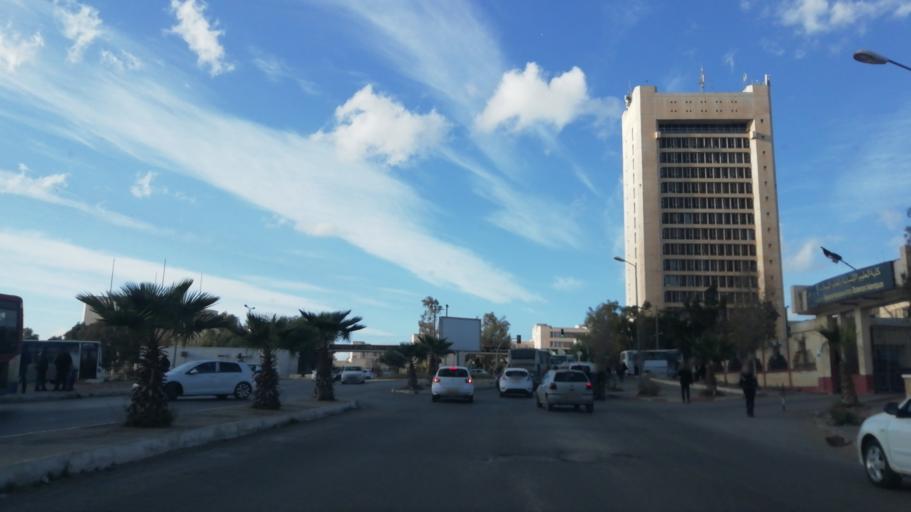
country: DZ
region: Oran
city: Bir el Djir
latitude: 35.7033
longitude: -0.5770
